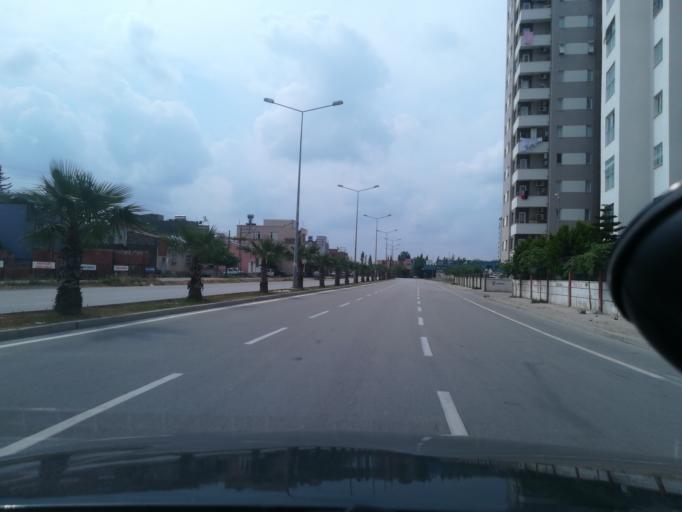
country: TR
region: Adana
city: Seyhan
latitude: 37.0035
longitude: 35.2585
